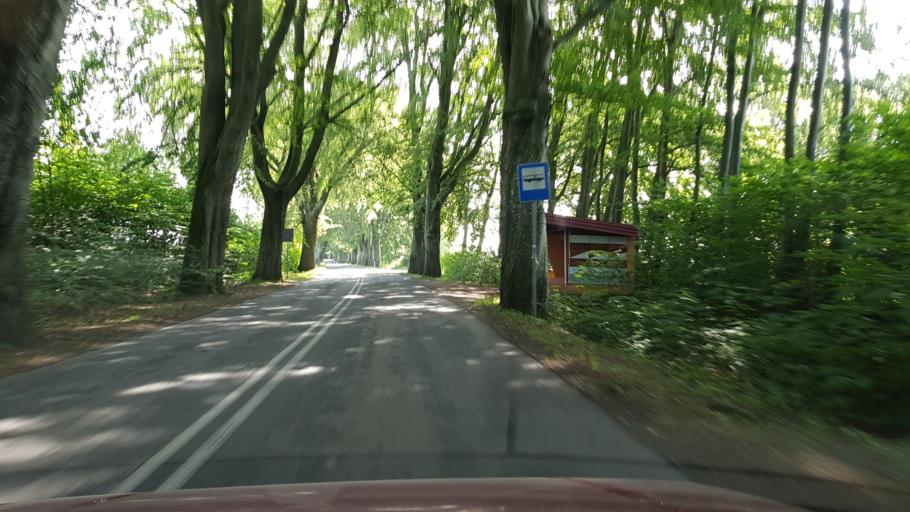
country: PL
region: West Pomeranian Voivodeship
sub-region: Powiat koszalinski
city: Polanow
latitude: 54.1377
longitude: 16.5858
